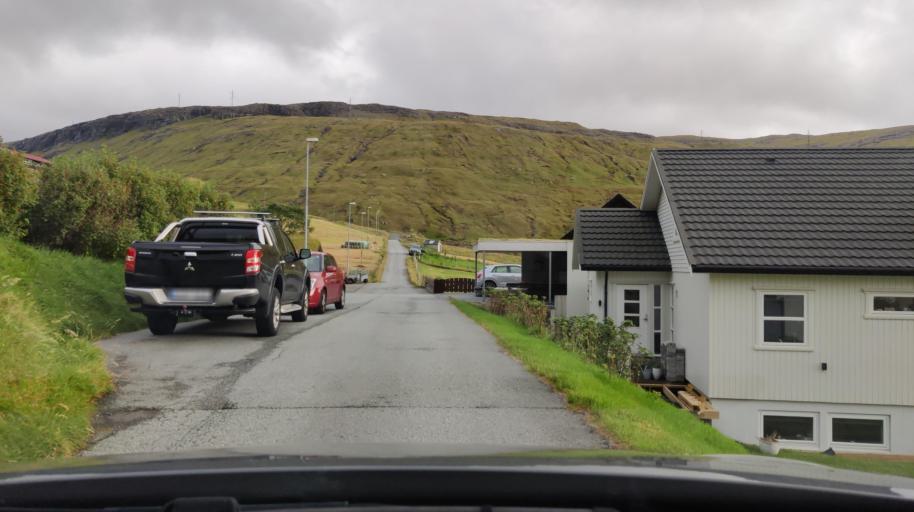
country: FO
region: Streymoy
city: Vestmanna
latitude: 62.1540
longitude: -7.1432
